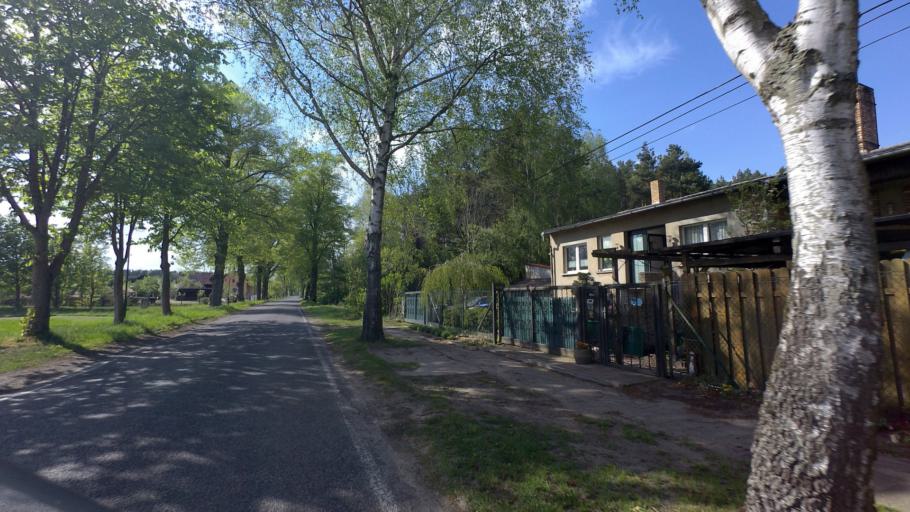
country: DE
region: Brandenburg
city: Templin
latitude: 53.0027
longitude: 13.4754
